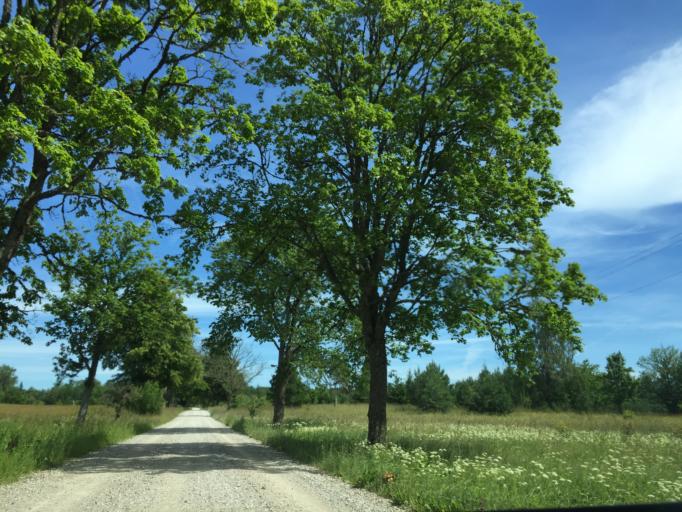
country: LV
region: Dundaga
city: Dundaga
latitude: 57.6206
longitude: 22.2902
